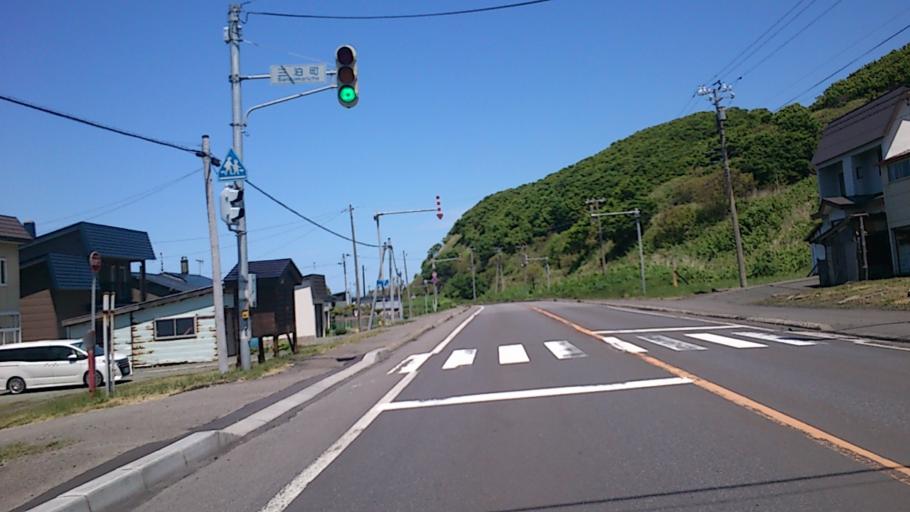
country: JP
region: Hokkaido
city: Rumoi
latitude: 43.9694
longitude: 141.6466
